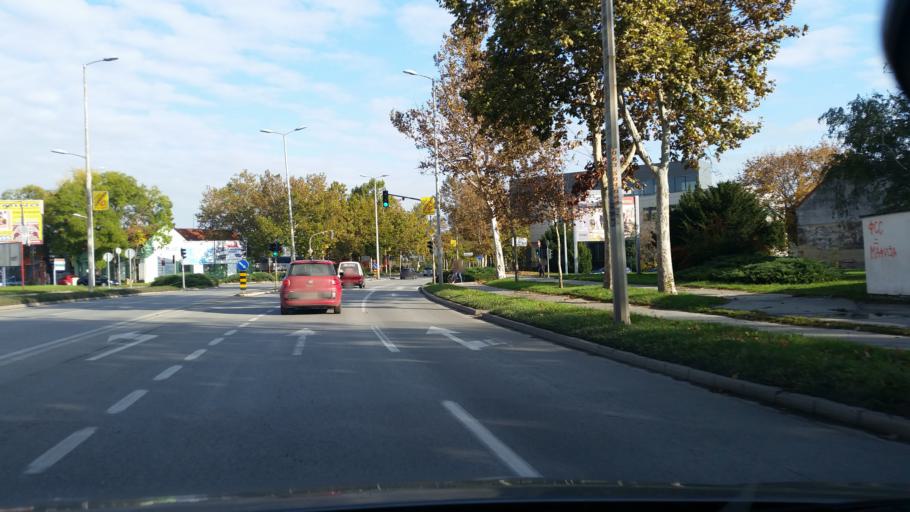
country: RS
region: Autonomna Pokrajina Vojvodina
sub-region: Srednjebanatski Okrug
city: Zrenjanin
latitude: 45.3835
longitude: 20.3928
